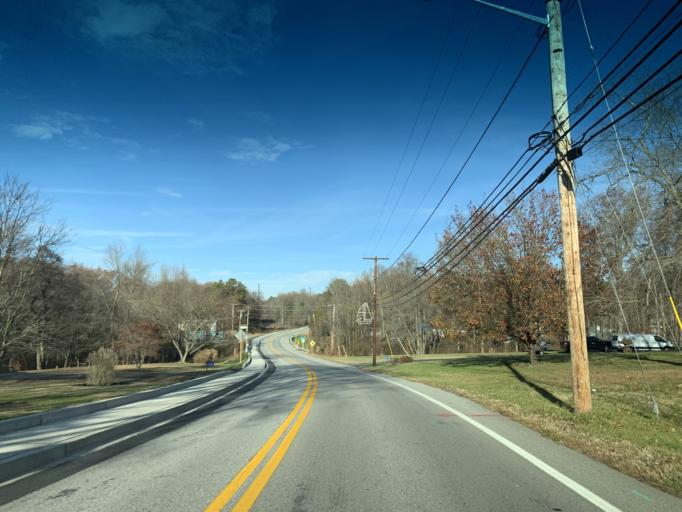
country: US
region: Maryland
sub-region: Cecil County
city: Charlestown
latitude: 39.5774
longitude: -75.9733
